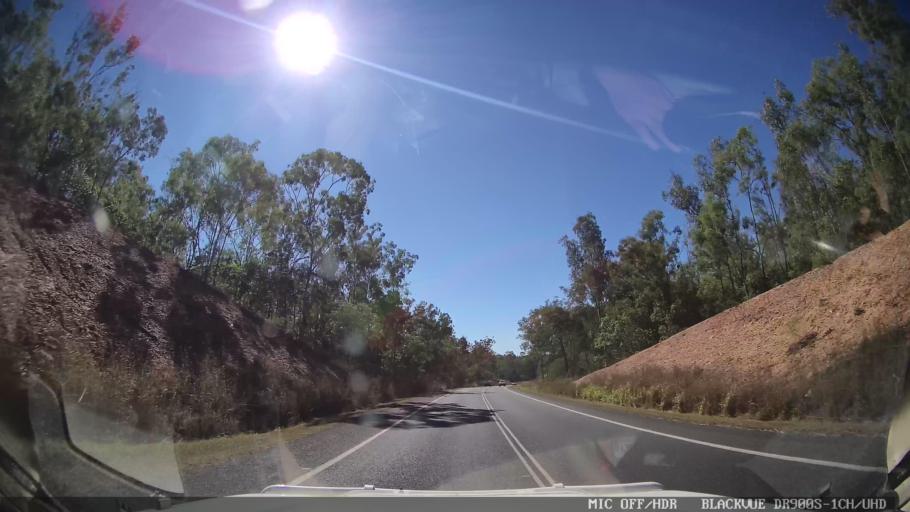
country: AU
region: Queensland
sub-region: Gladstone
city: Toolooa
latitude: -23.9644
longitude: 151.2175
